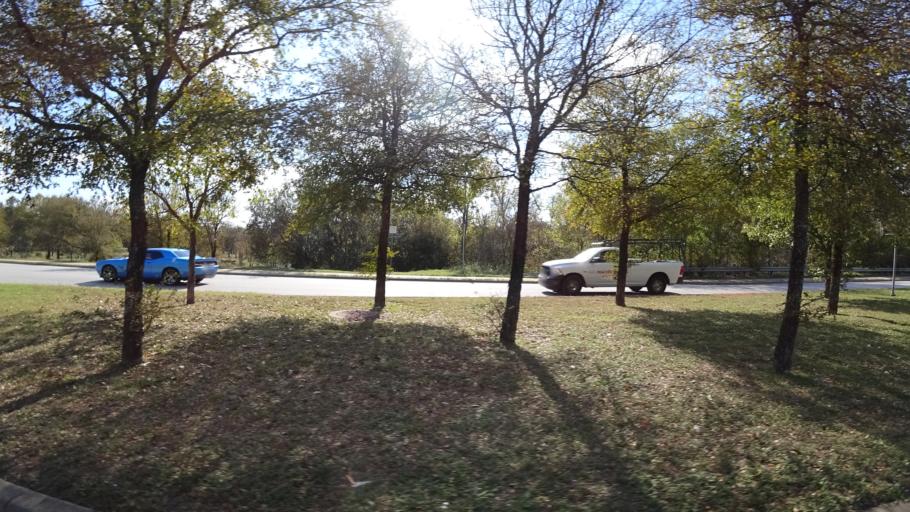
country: US
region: Texas
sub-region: Travis County
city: Shady Hollow
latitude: 30.1842
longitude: -97.8512
